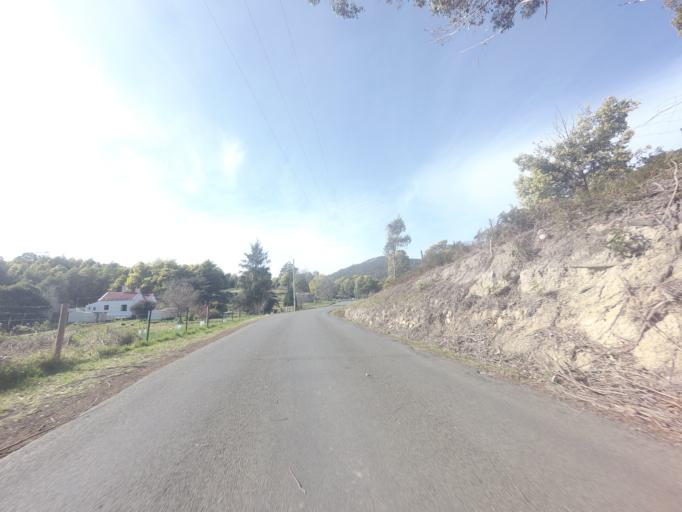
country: AU
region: Tasmania
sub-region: Huon Valley
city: Cygnet
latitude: -43.1743
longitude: 147.1594
